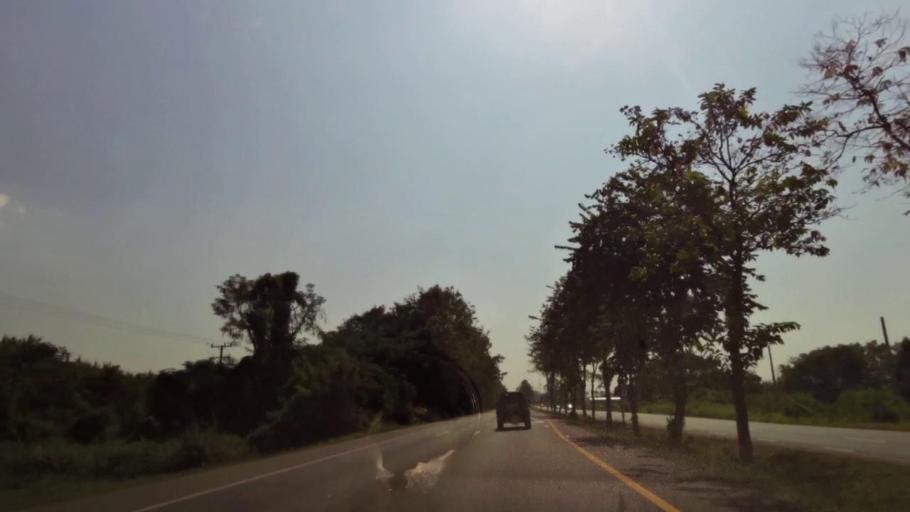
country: TH
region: Phichit
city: Bueng Na Rang
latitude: 16.0921
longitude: 100.1252
